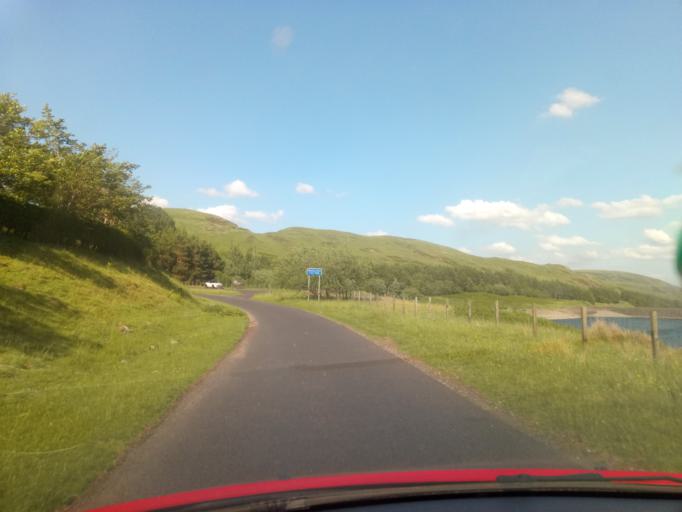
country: GB
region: Scotland
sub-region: The Scottish Borders
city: Peebles
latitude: 55.4959
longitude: -3.2599
